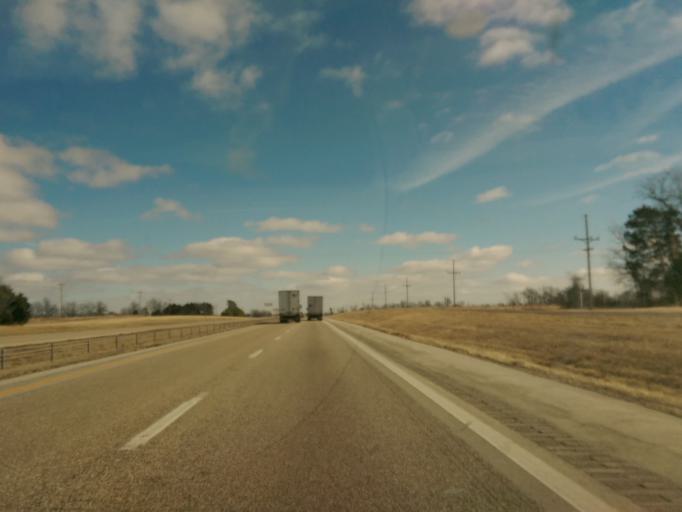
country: US
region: Missouri
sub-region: Montgomery County
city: Montgomery City
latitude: 38.9063
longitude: -91.5146
